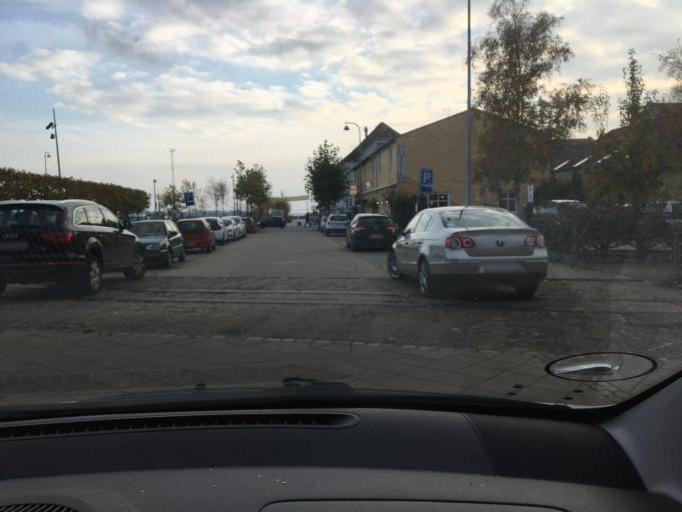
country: DK
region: South Denmark
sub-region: Fredericia Kommune
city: Fredericia
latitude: 55.5624
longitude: 9.7566
